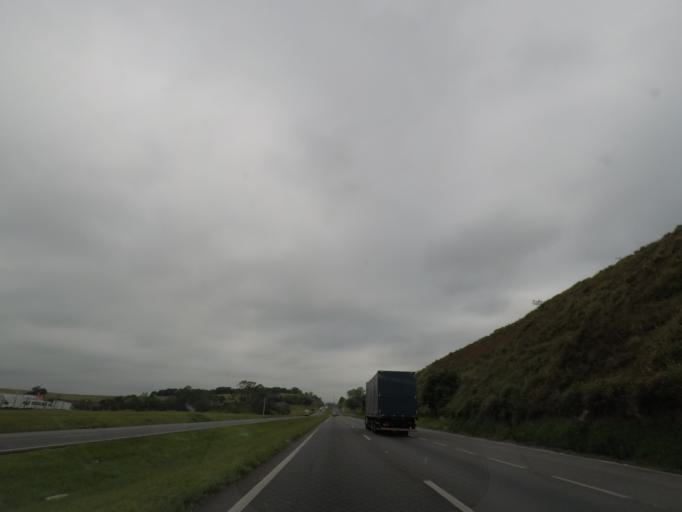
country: BR
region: Sao Paulo
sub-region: Itatiba
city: Itatiba
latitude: -22.9944
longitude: -46.7916
